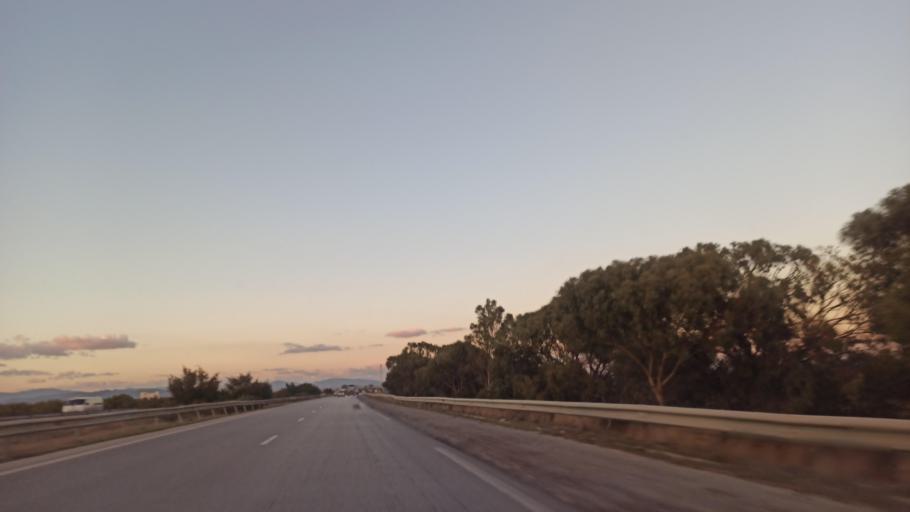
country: TN
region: Nabul
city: Al Hammamat
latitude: 36.2563
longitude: 10.4274
